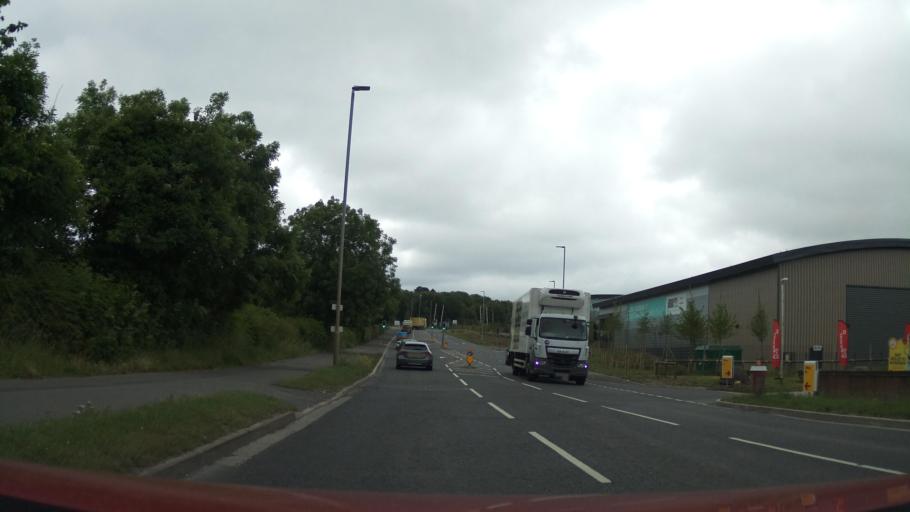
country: GB
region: England
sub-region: Leicestershire
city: Coalville
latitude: 52.7129
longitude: -1.3449
